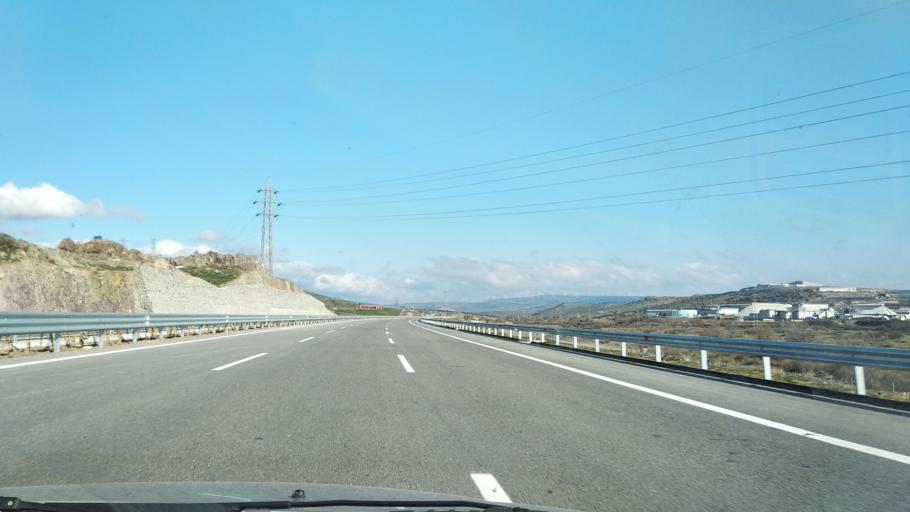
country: TR
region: Izmir
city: Aliaga
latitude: 38.8238
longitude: 27.0323
